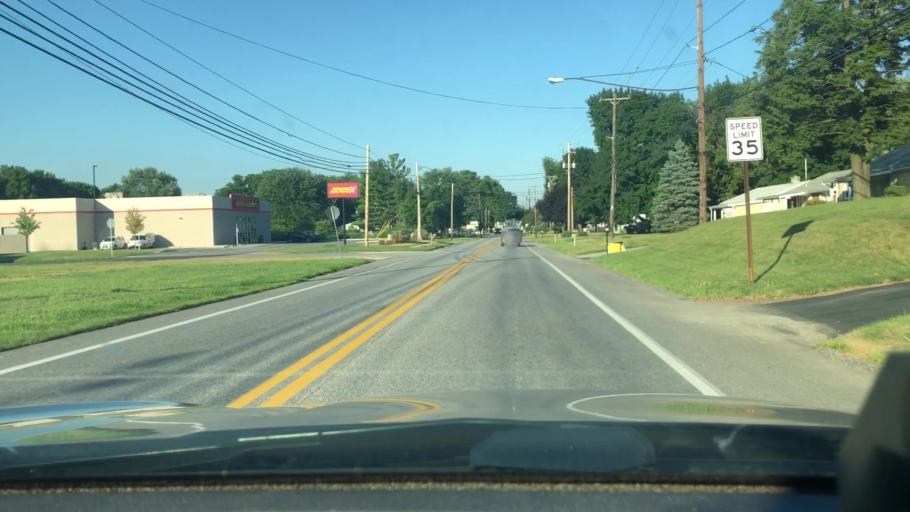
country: US
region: Pennsylvania
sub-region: Cumberland County
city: Mechanicsburg
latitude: 40.2164
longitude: -76.9893
